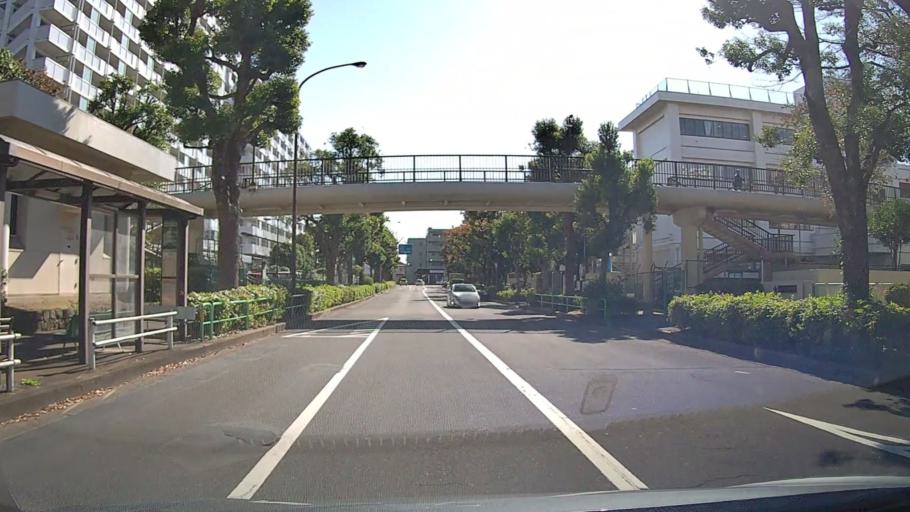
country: JP
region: Saitama
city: Wako
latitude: 35.7554
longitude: 139.6266
